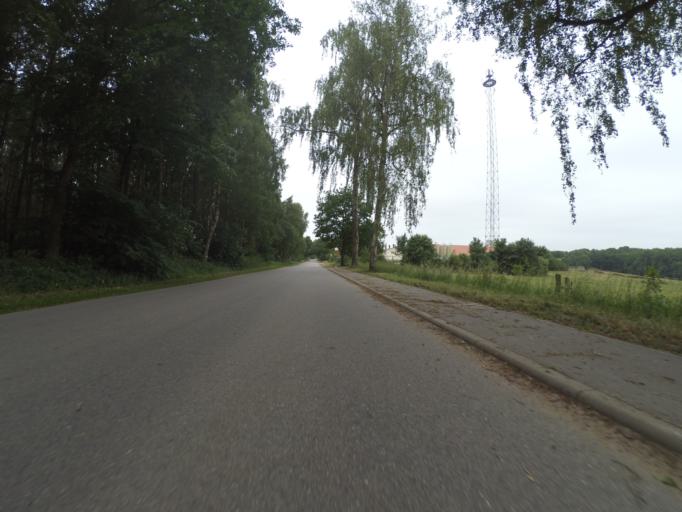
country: DE
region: Mecklenburg-Vorpommern
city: Goldberg
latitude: 53.5450
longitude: 12.0494
